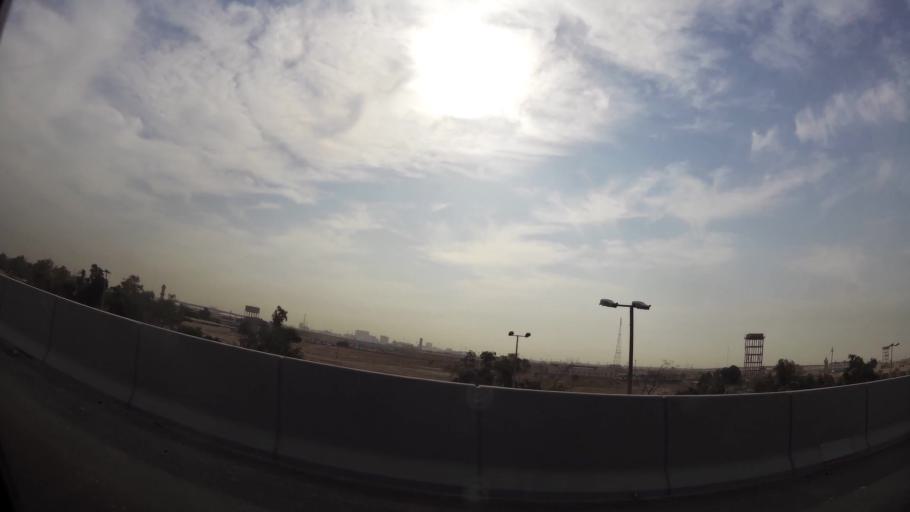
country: KW
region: Al Asimah
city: Ar Rabiyah
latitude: 29.3208
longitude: 47.8857
